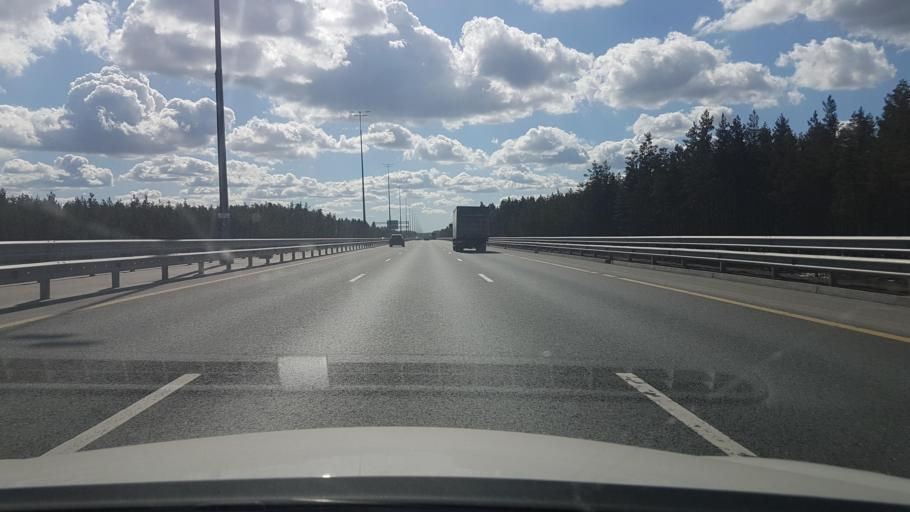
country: RU
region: Leningrad
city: Krasnyy Bor
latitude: 59.6264
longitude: 30.6554
